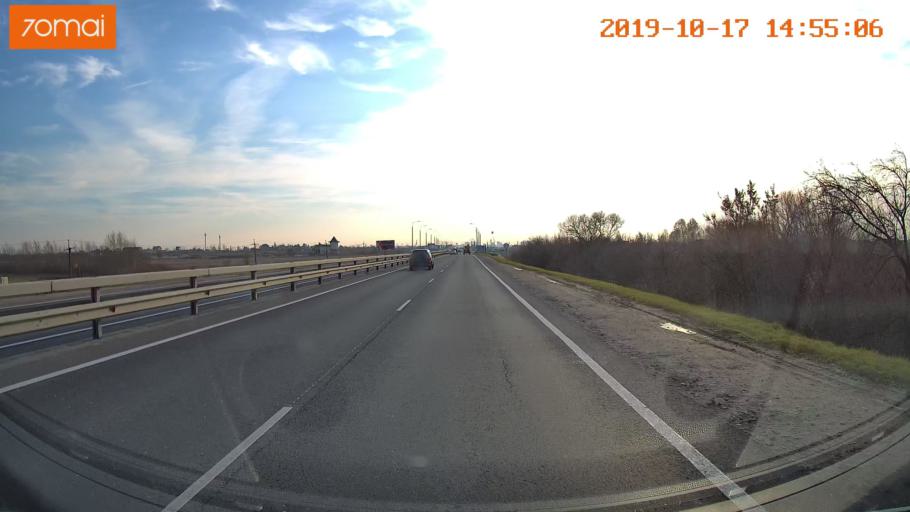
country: RU
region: Rjazan
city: Polyany
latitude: 54.6725
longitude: 39.8274
